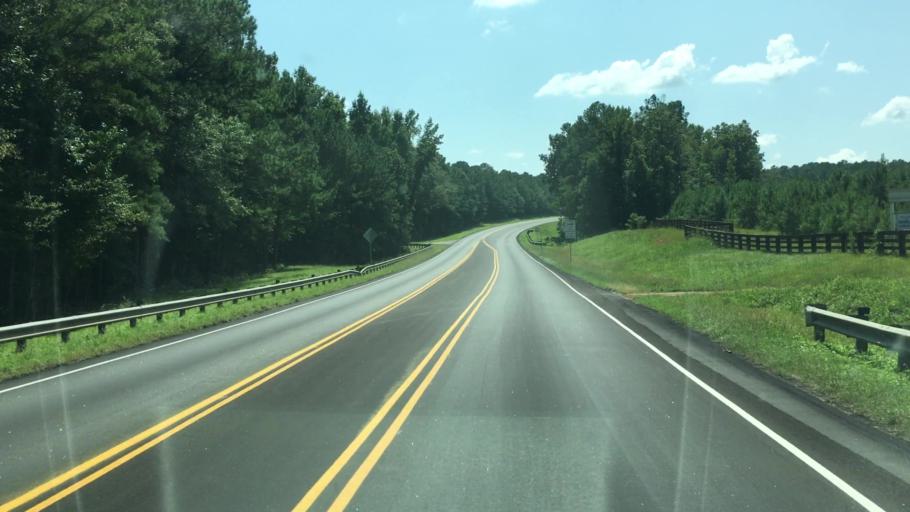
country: US
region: Georgia
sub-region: Morgan County
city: Madison
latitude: 33.7180
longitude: -83.4350
